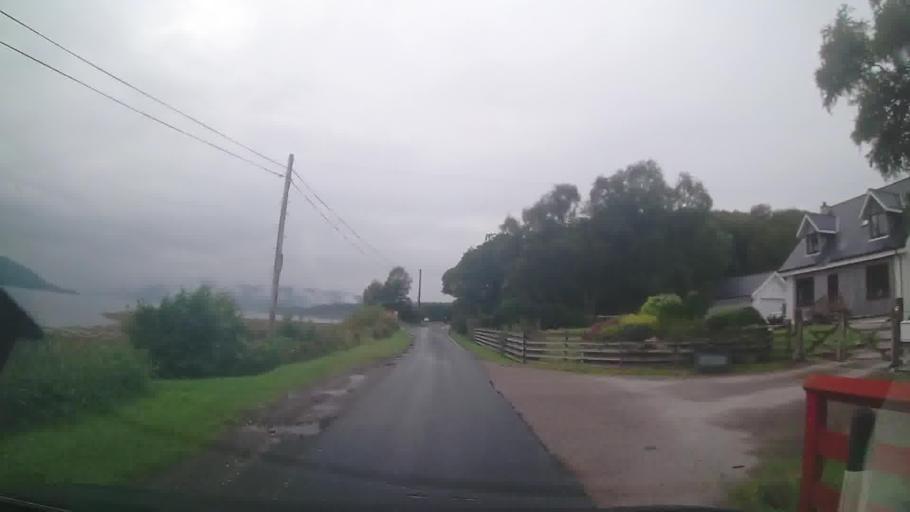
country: GB
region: Scotland
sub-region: Argyll and Bute
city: Isle Of Mull
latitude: 56.7099
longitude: -5.7179
